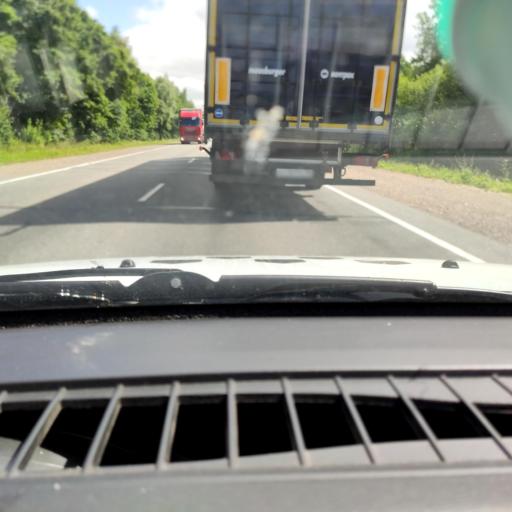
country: RU
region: Udmurtiya
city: Pychas
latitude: 56.4800
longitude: 52.5309
